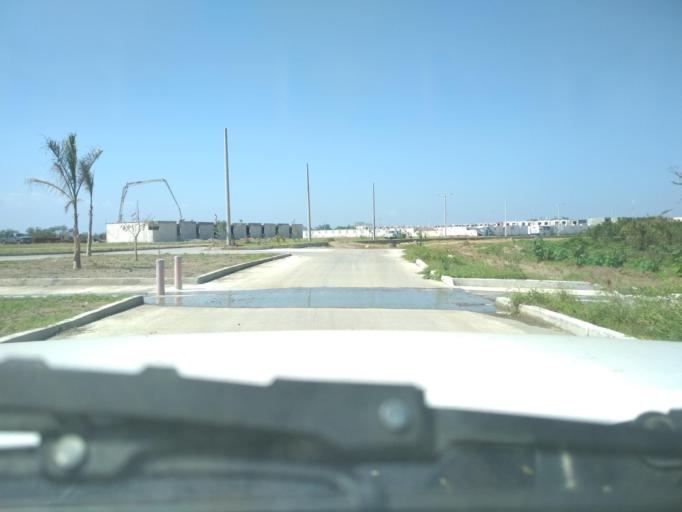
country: MX
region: Veracruz
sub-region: Medellin
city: Fraccionamiento Arboledas San Ramon
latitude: 19.1007
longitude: -96.1667
